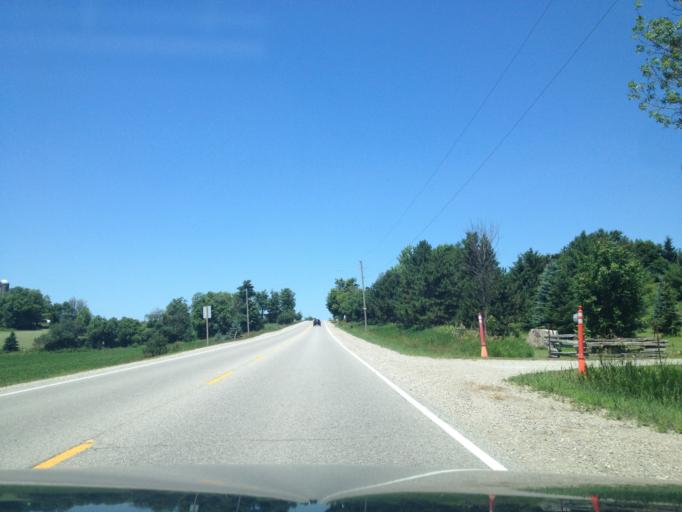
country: CA
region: Ontario
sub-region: Wellington County
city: Guelph
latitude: 43.6197
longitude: -80.2198
